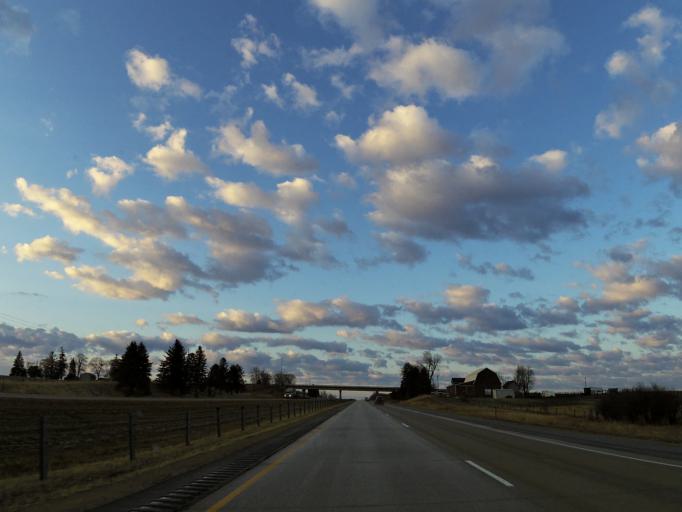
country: US
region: Minnesota
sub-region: Rice County
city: Dundas
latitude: 44.4024
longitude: -93.2927
